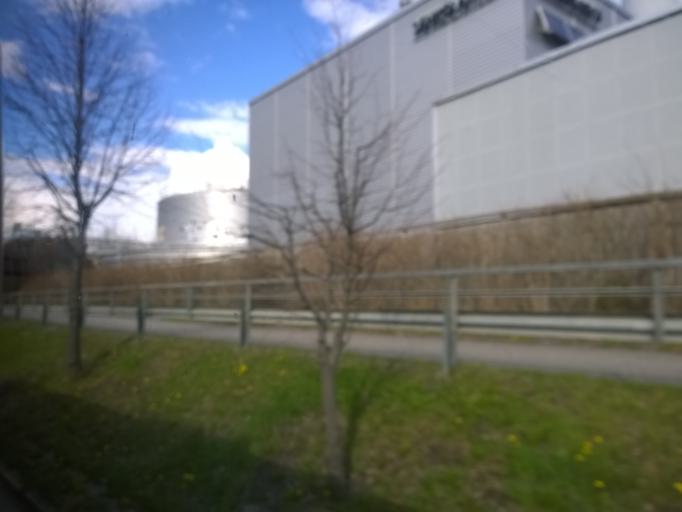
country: FI
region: Pirkanmaa
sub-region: Tampere
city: Tampere
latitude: 61.4789
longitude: 23.7751
